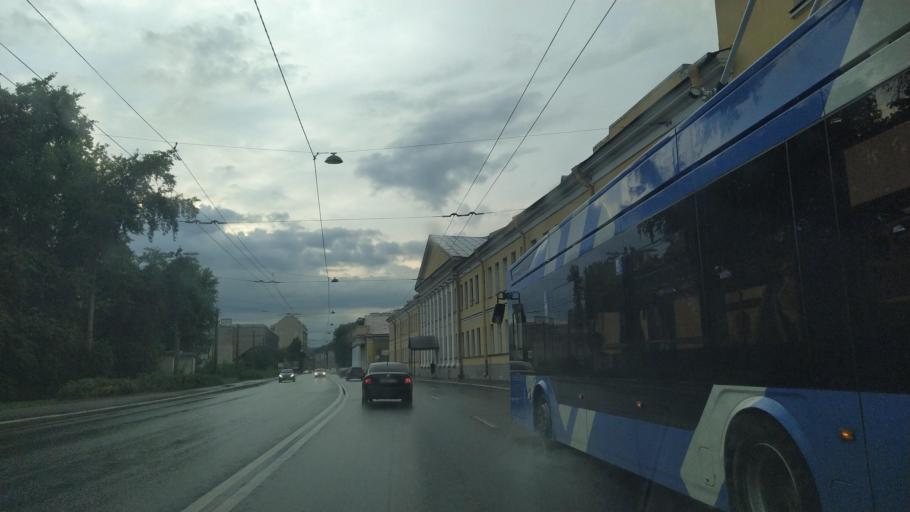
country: RU
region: St.-Petersburg
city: Petrogradka
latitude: 59.9558
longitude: 30.2842
